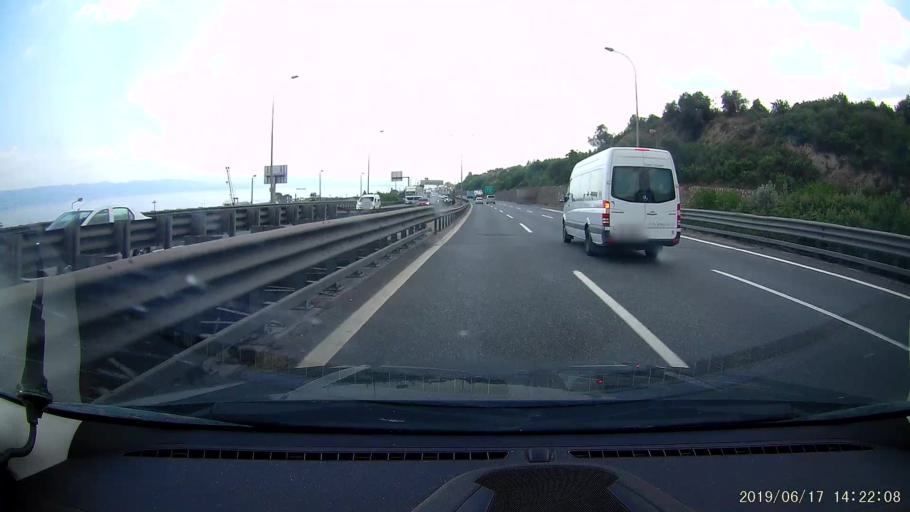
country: TR
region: Kocaeli
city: Hereke
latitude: 40.7781
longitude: 29.5956
